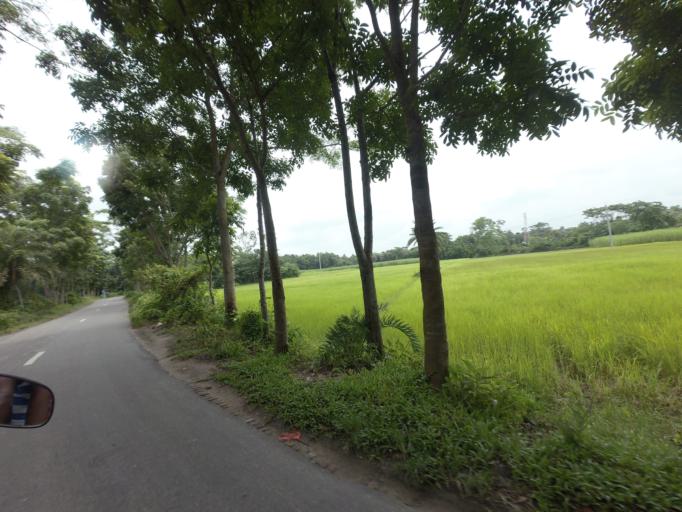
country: BD
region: Khulna
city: Kalia
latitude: 23.0975
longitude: 89.6507
